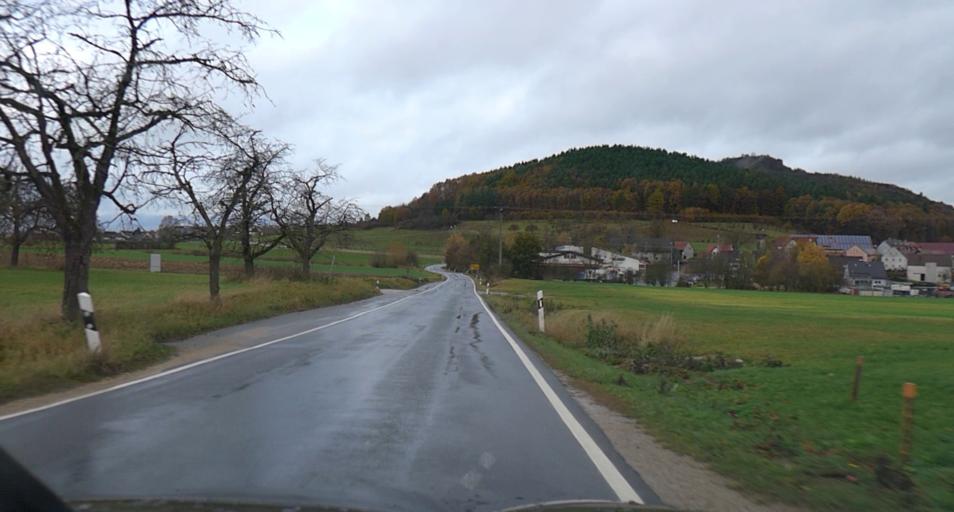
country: DE
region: Bavaria
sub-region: Upper Franconia
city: Leutenbach
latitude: 49.6981
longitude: 11.1618
